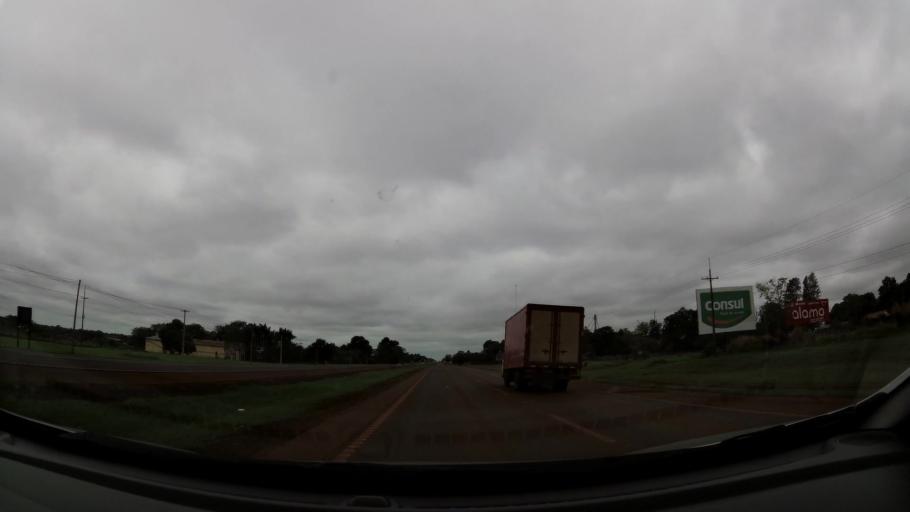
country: PY
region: Alto Parana
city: Colonia Yguazu
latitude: -25.4873
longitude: -54.8474
